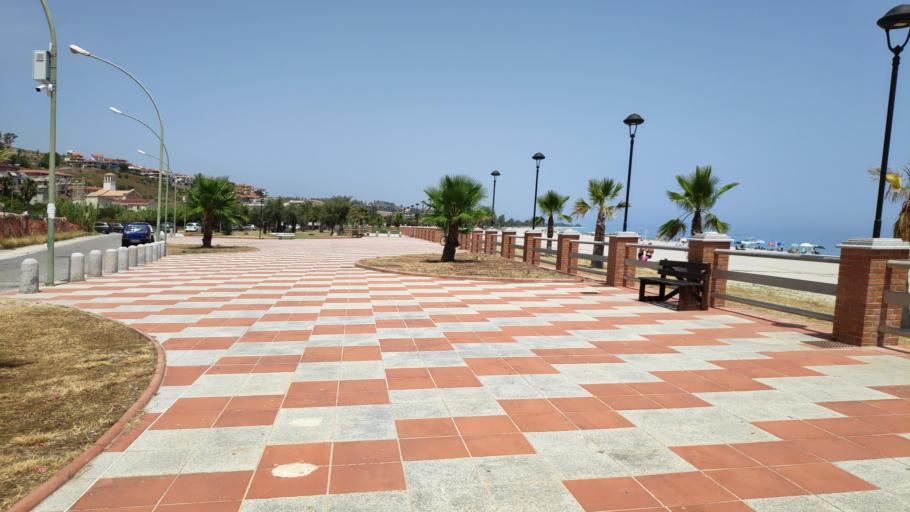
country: IT
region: Calabria
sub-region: Provincia di Catanzaro
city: Santa Caterina dello Ionio Marina
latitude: 38.5272
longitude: 16.5725
